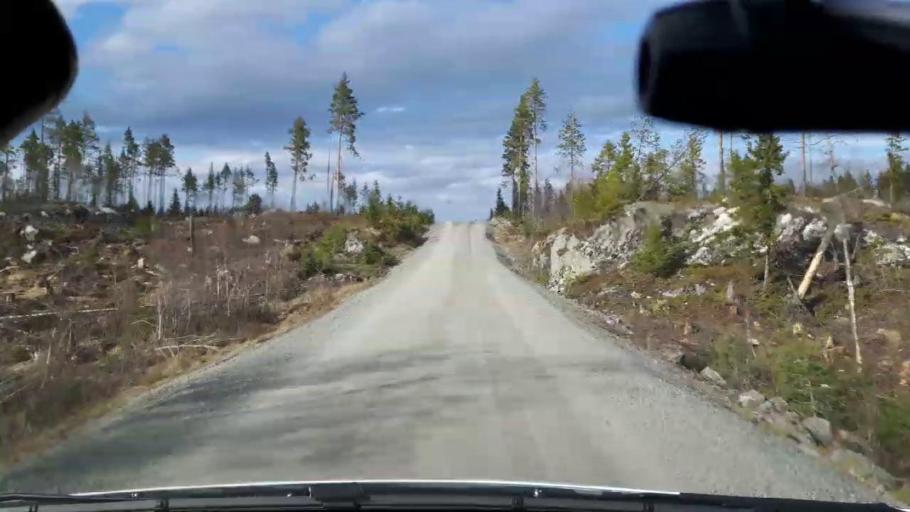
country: SE
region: Jaemtland
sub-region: Bergs Kommun
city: Hoverberg
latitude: 62.9255
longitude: 14.6434
